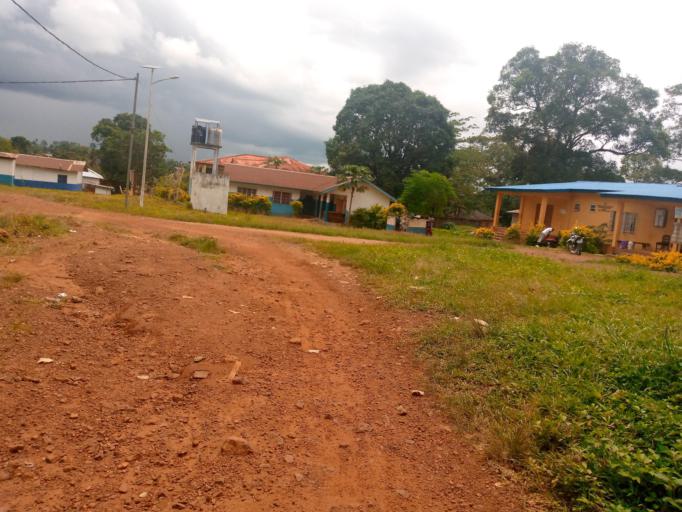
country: SL
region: Southern Province
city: Mogbwemo
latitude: 7.6042
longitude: -12.1736
